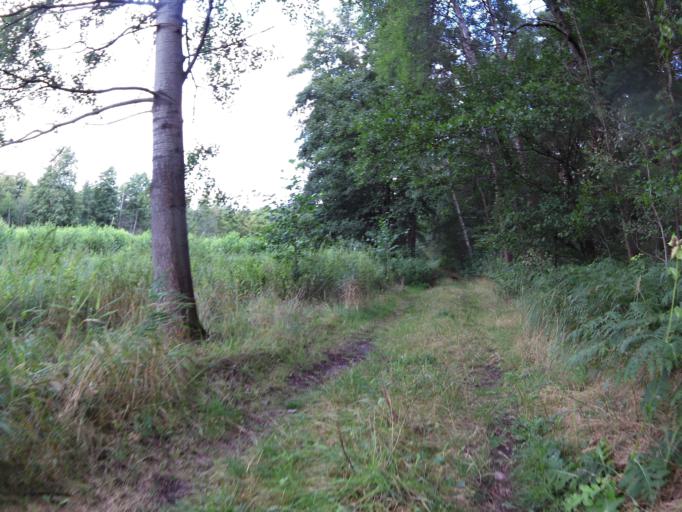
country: DE
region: Brandenburg
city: Munchehofe
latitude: 52.1856
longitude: 13.8990
